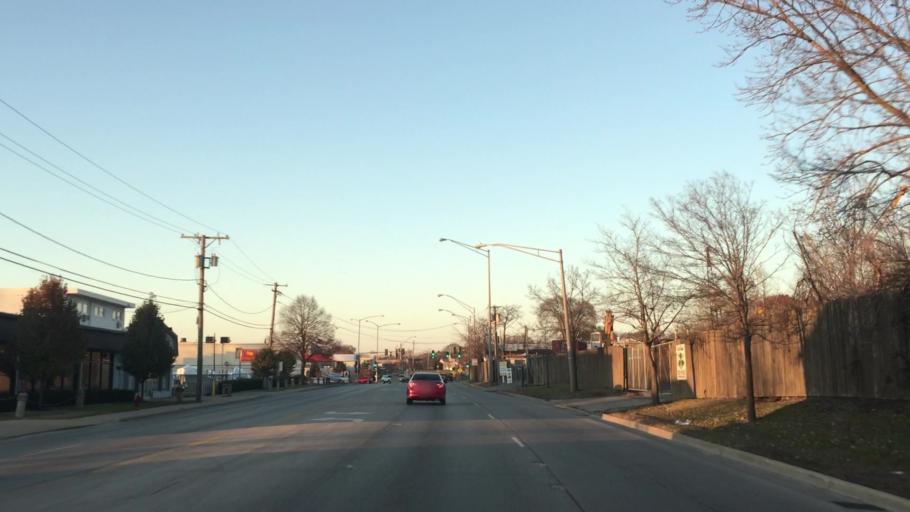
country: US
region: Illinois
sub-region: Kane County
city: Aurora
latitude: 41.7690
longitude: -88.3063
